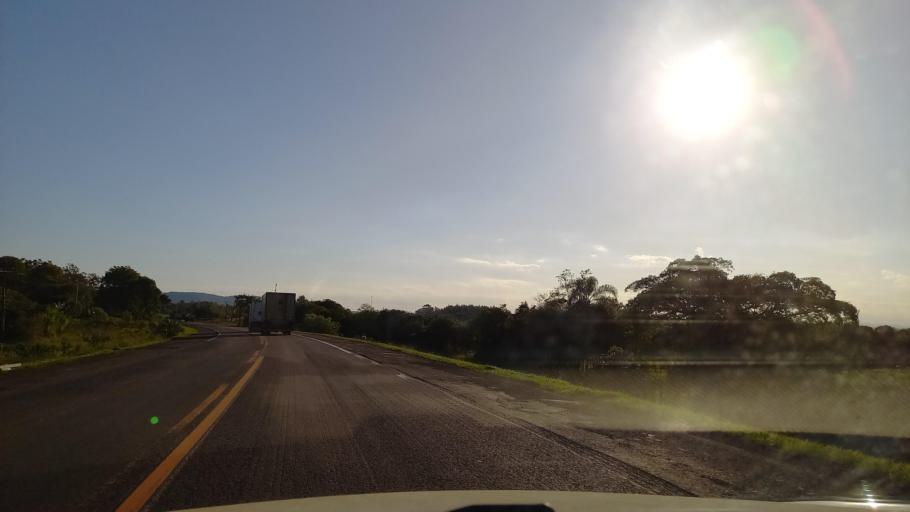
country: BR
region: Rio Grande do Sul
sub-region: Venancio Aires
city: Venancio Aires
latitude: -29.6682
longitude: -52.0299
